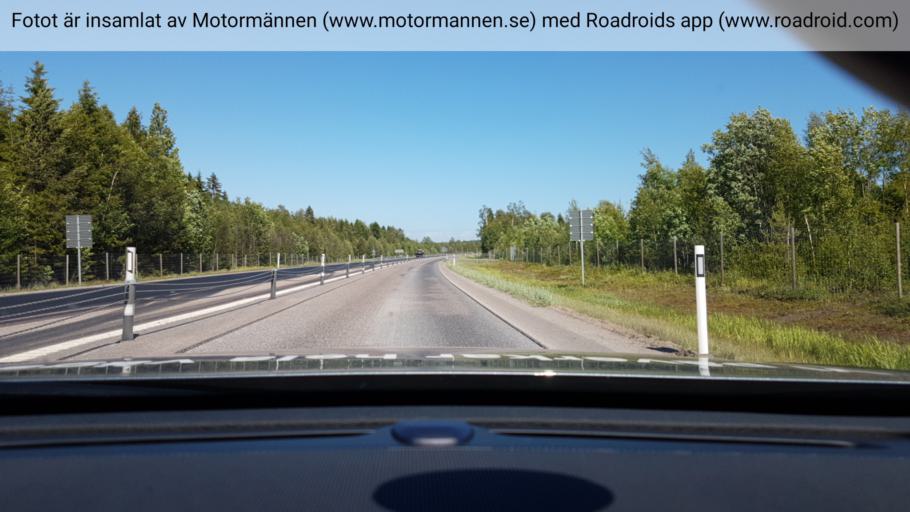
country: SE
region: Vaesterbotten
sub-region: Nordmalings Kommun
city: Nordmaling
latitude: 63.5653
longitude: 19.4310
